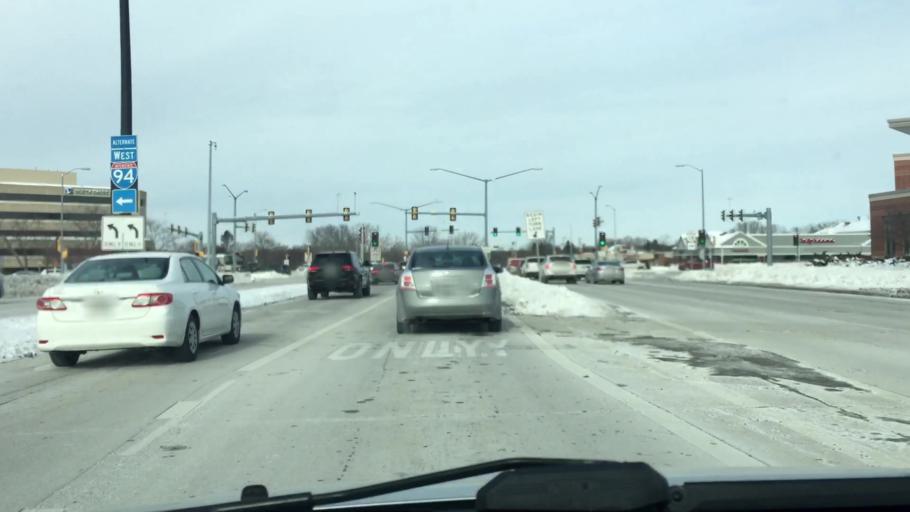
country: US
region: Wisconsin
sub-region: Waukesha County
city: Brookfield
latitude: 43.0350
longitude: -88.1068
